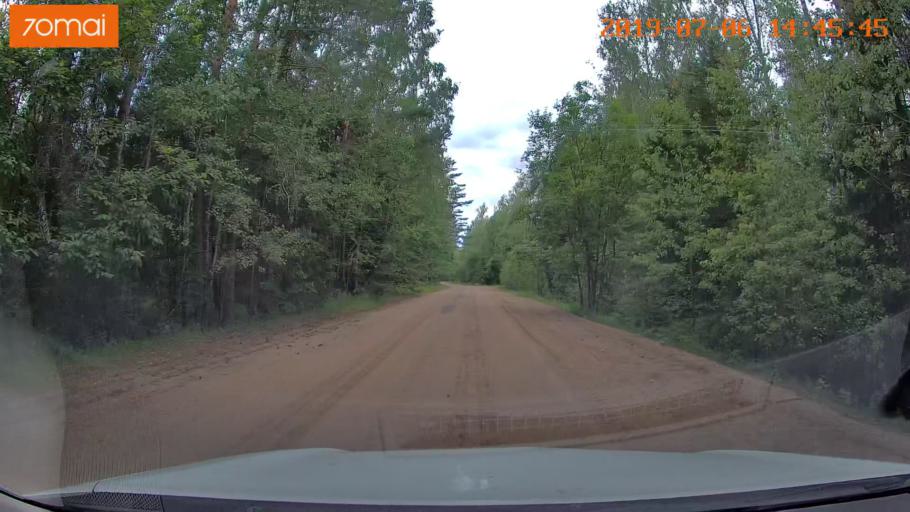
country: BY
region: Minsk
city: Ivyanyets
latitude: 53.9747
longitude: 26.6846
